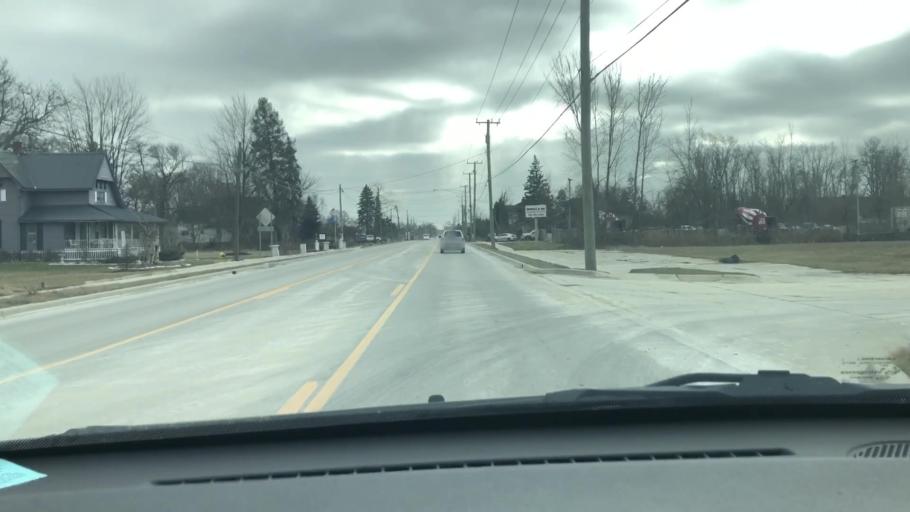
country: US
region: Michigan
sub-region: Macomb County
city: Shelby
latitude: 42.7330
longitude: -83.0363
